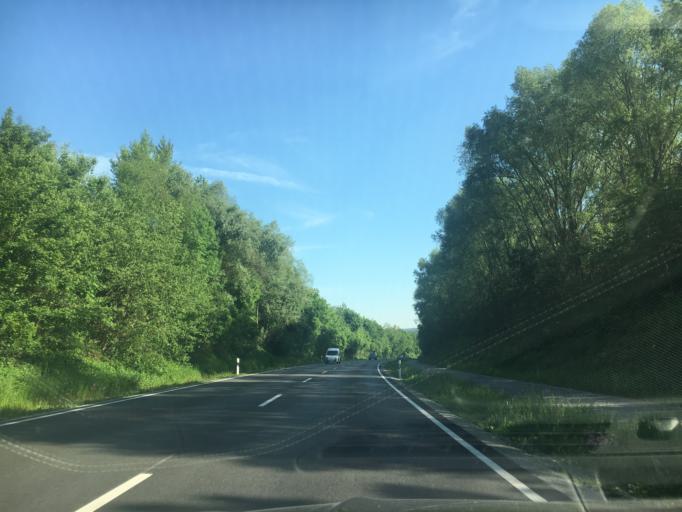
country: DE
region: Bavaria
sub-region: Upper Bavaria
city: Altoetting
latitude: 48.2393
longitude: 12.6539
